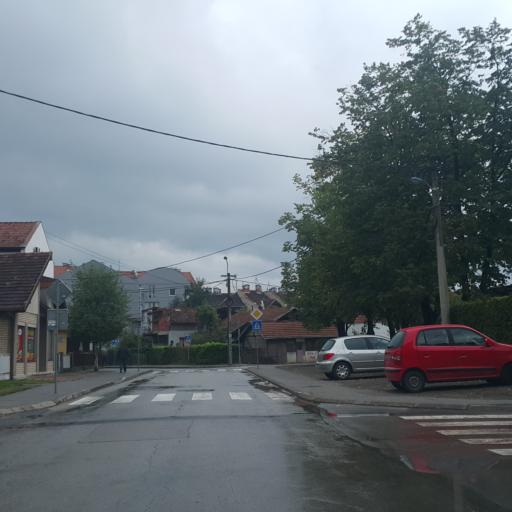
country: RS
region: Central Serbia
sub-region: Rasinski Okrug
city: Krusevac
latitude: 43.5744
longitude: 21.3399
